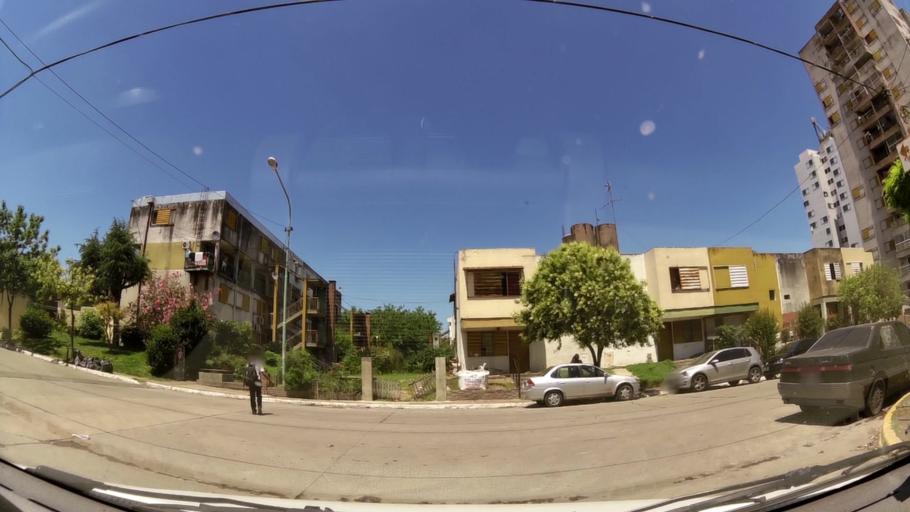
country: AR
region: Buenos Aires
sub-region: Partido de Merlo
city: Merlo
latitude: -34.6529
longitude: -58.7087
